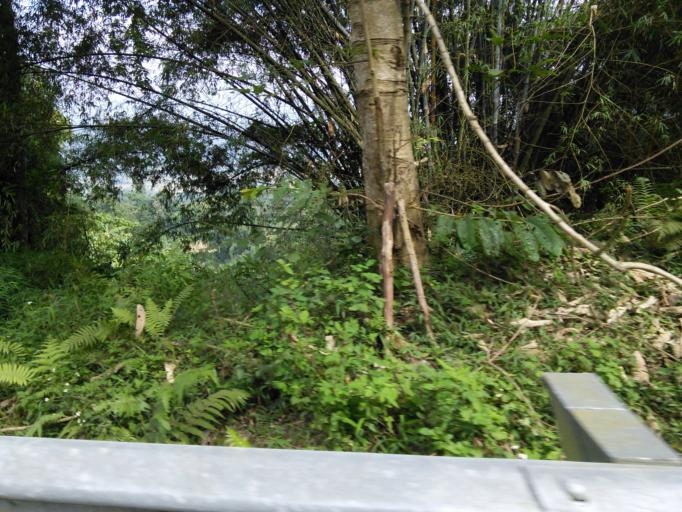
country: VN
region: Lao Cai
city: Lao Cai
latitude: 22.4485
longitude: 103.9341
